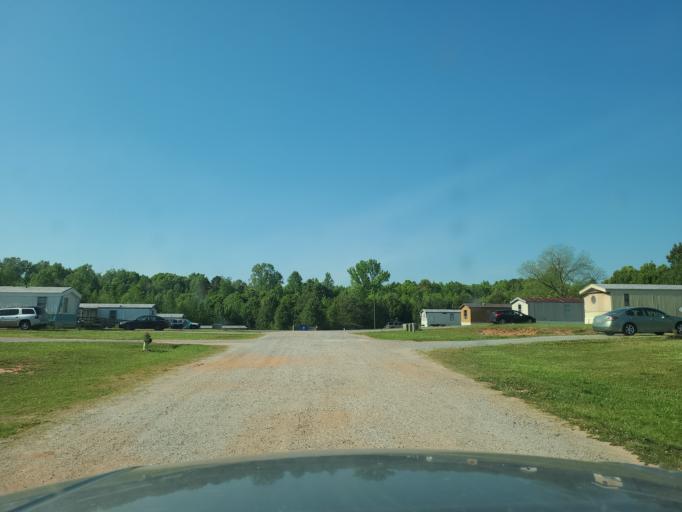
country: US
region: North Carolina
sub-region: Cleveland County
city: Shelby
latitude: 35.2241
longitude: -81.5319
